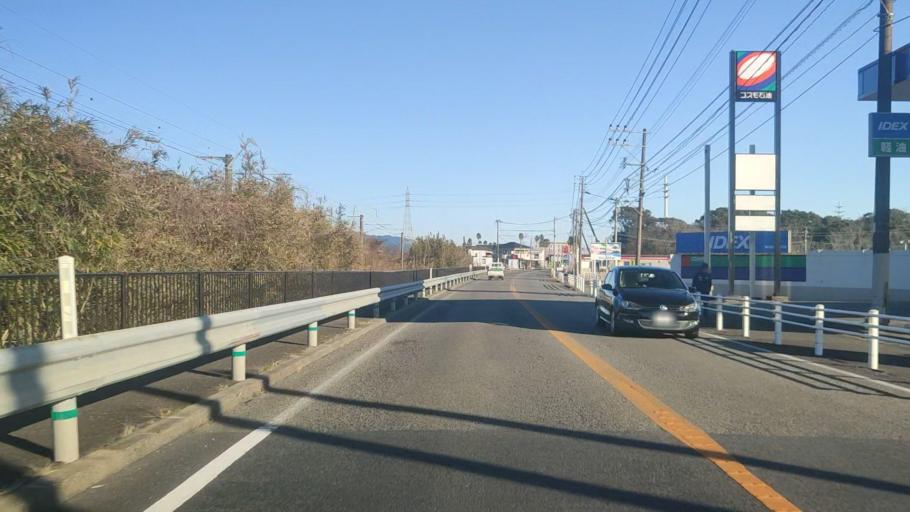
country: JP
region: Miyazaki
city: Nobeoka
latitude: 32.3890
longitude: 131.6275
